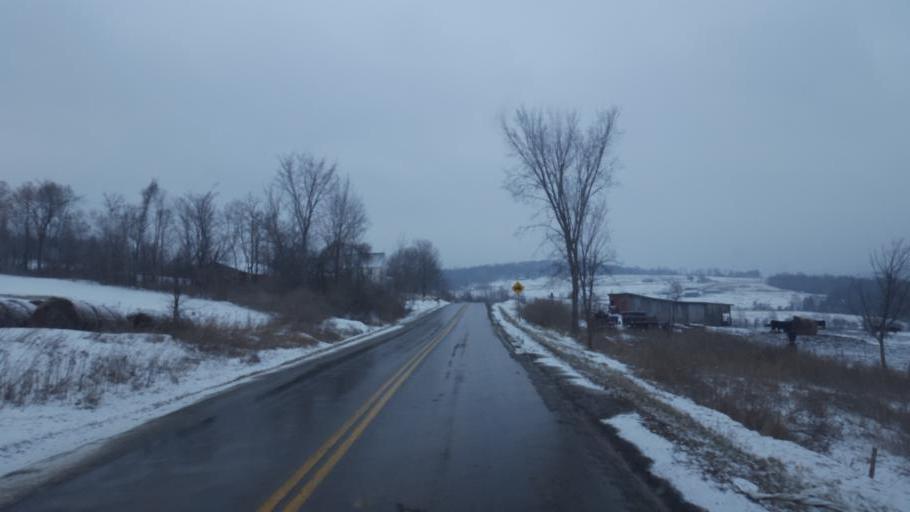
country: US
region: Pennsylvania
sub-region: Tioga County
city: Elkland
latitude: 42.0818
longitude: -77.4480
